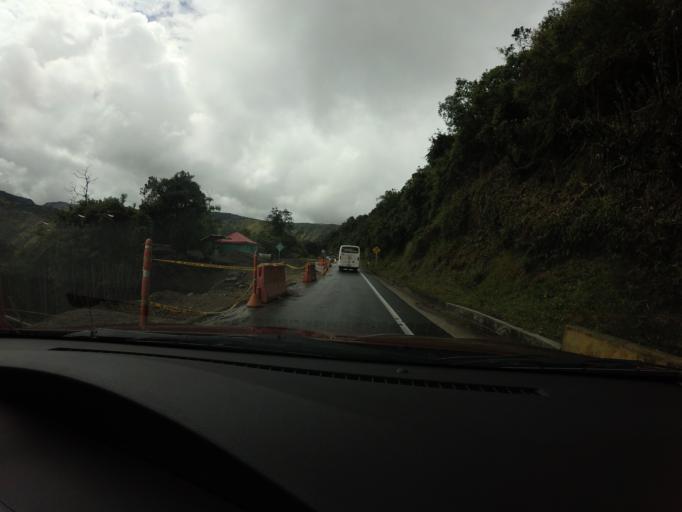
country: CO
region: Tolima
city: Herveo
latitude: 5.0660
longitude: -75.2986
